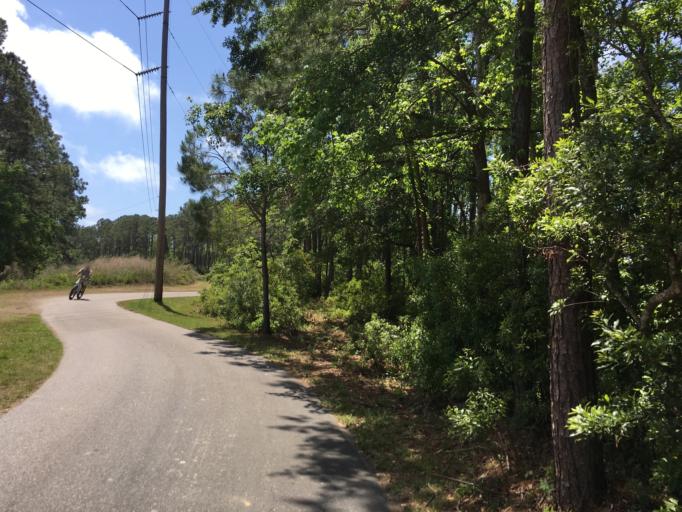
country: US
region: South Carolina
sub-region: Beaufort County
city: Hilton Head Island
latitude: 32.1674
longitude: -80.7673
